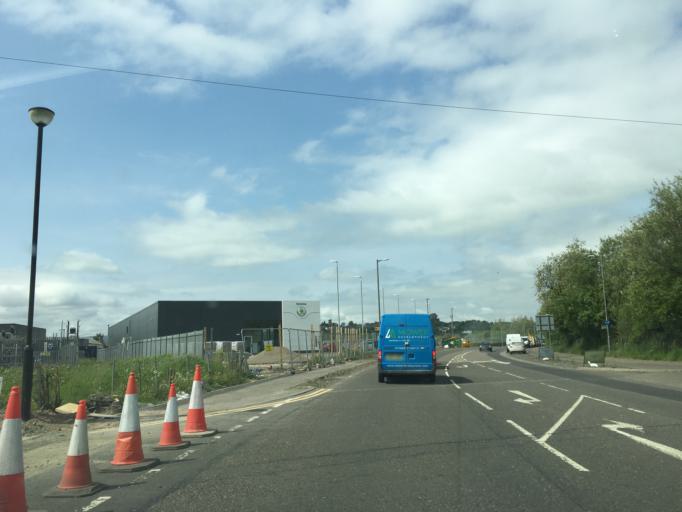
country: GB
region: Scotland
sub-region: Stirling
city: Stirling
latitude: 56.1180
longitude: -3.9183
